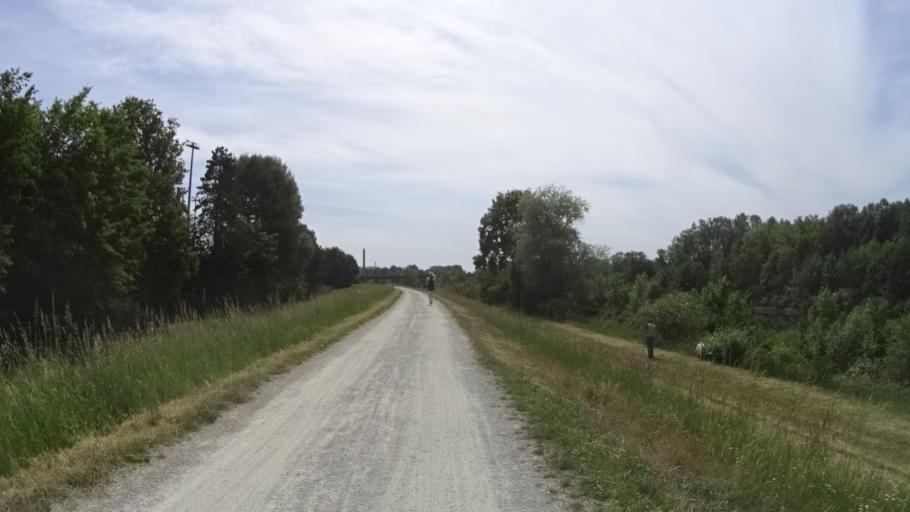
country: DE
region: Bavaria
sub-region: Lower Bavaria
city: Kelheim
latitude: 48.9122
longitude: 11.8860
